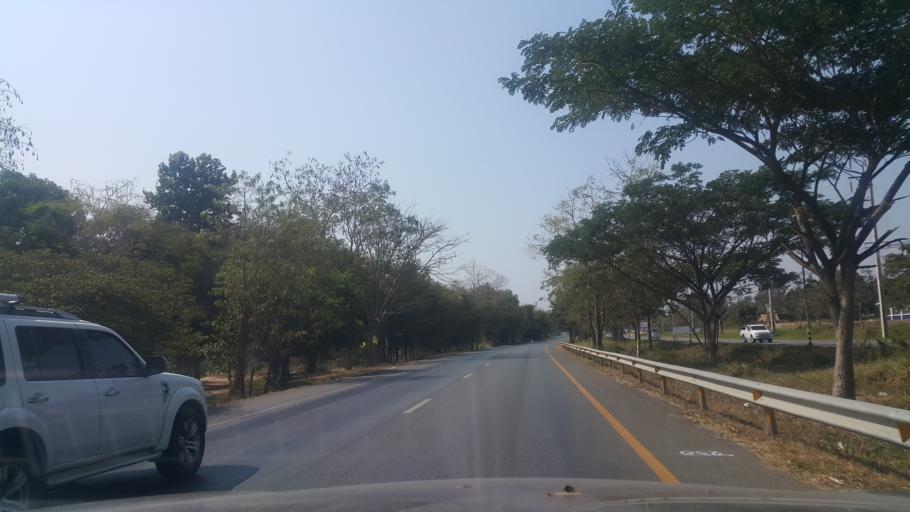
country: TH
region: Nakhon Ratchasima
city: Pak Thong Chai
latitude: 14.5935
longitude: 102.0015
